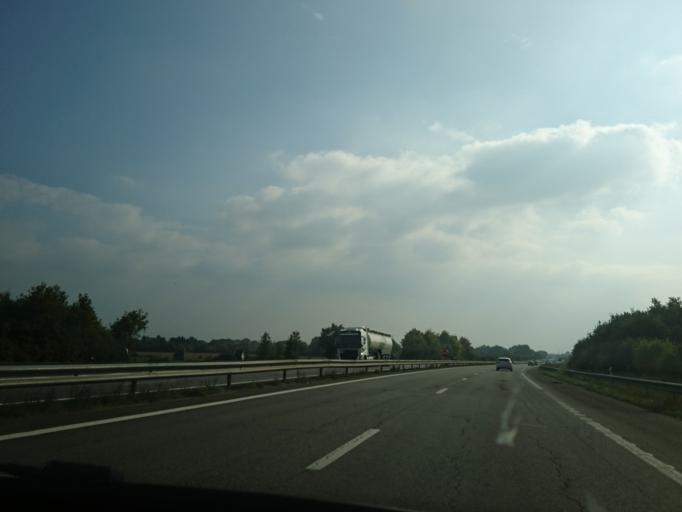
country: FR
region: Pays de la Loire
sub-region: Departement de la Loire-Atlantique
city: Heric
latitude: 47.4626
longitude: -1.6385
